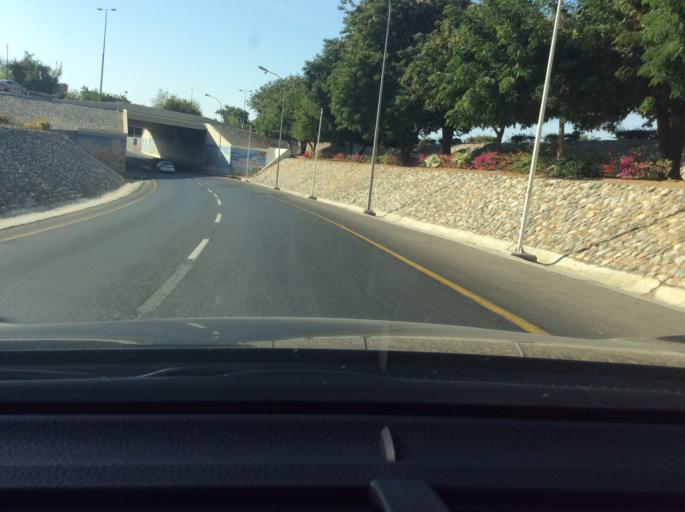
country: OM
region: Muhafazat Masqat
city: As Sib al Jadidah
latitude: 23.5874
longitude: 58.2573
